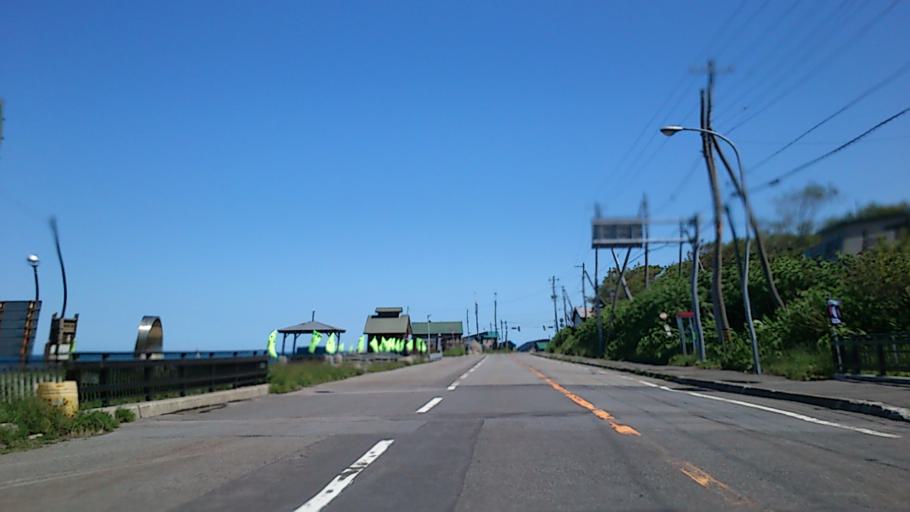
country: JP
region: Hokkaido
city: Rumoi
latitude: 43.7374
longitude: 141.3384
